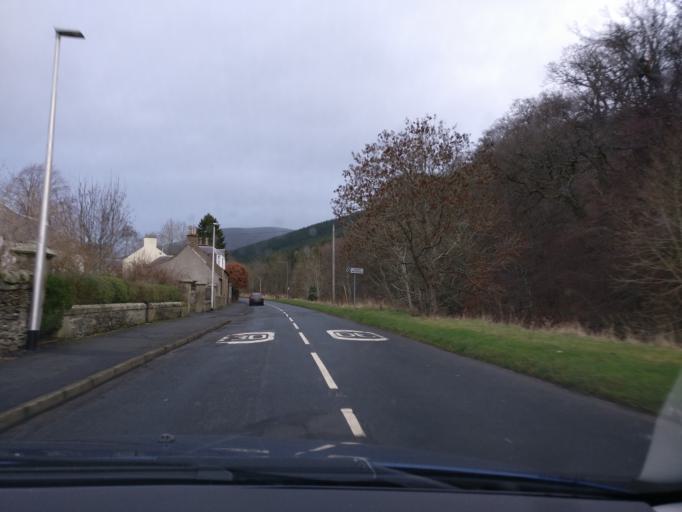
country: GB
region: Scotland
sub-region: The Scottish Borders
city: Innerleithen
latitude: 55.6245
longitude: -3.0600
